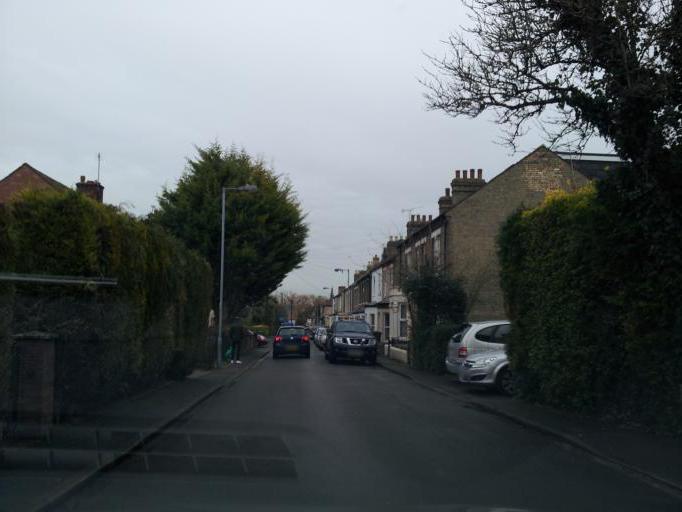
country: GB
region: England
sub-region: Cambridgeshire
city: Cambridge
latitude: 52.1955
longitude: 0.1541
